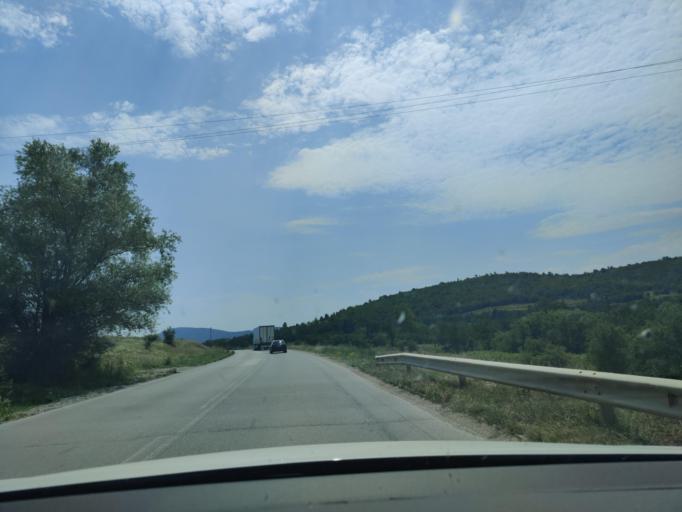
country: BG
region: Montana
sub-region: Obshtina Chiprovtsi
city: Chiprovtsi
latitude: 43.5098
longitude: 22.9804
